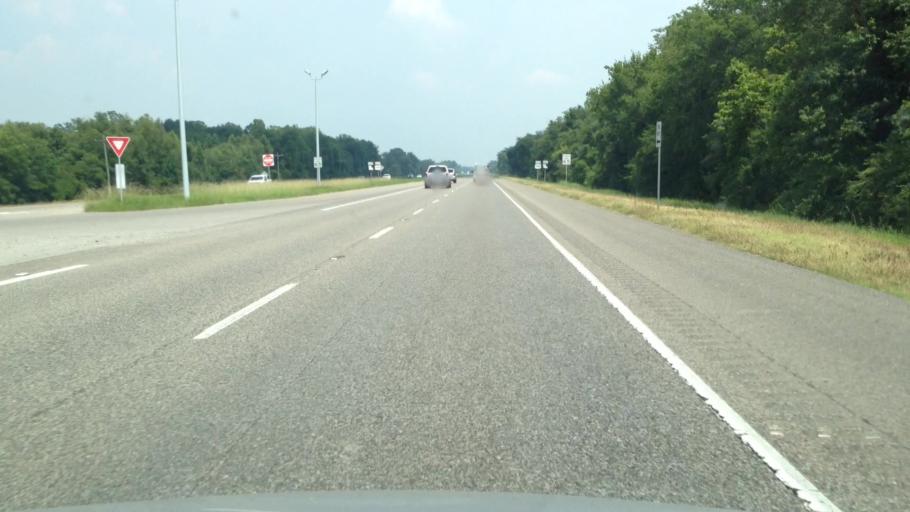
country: US
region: Louisiana
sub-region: West Baton Rouge Parish
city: Erwinville
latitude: 30.5187
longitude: -91.3649
